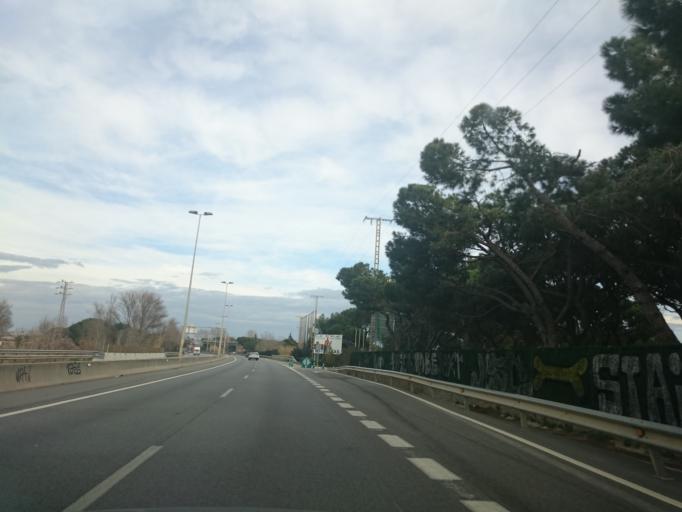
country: ES
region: Catalonia
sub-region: Provincia de Barcelona
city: Viladecans
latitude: 41.2724
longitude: 2.0417
